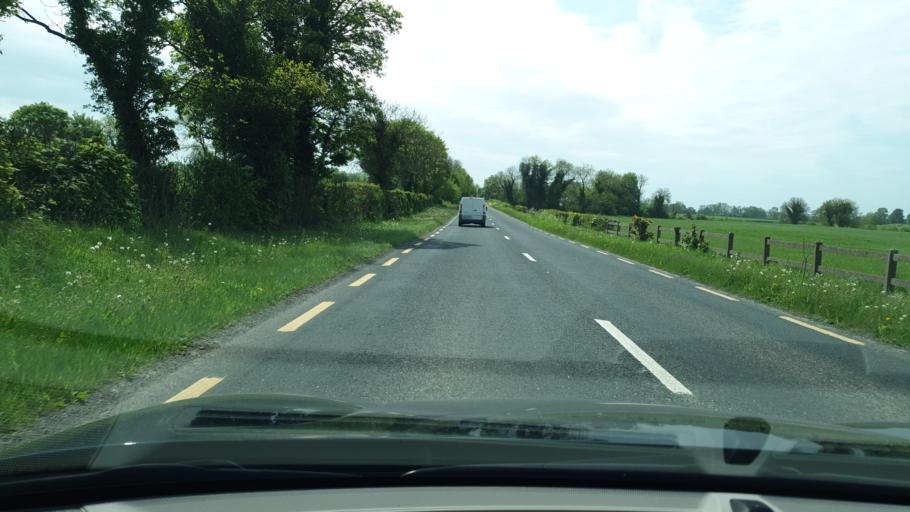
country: IE
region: Leinster
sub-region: An Mhi
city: Navan
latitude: 53.7626
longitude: -6.7250
